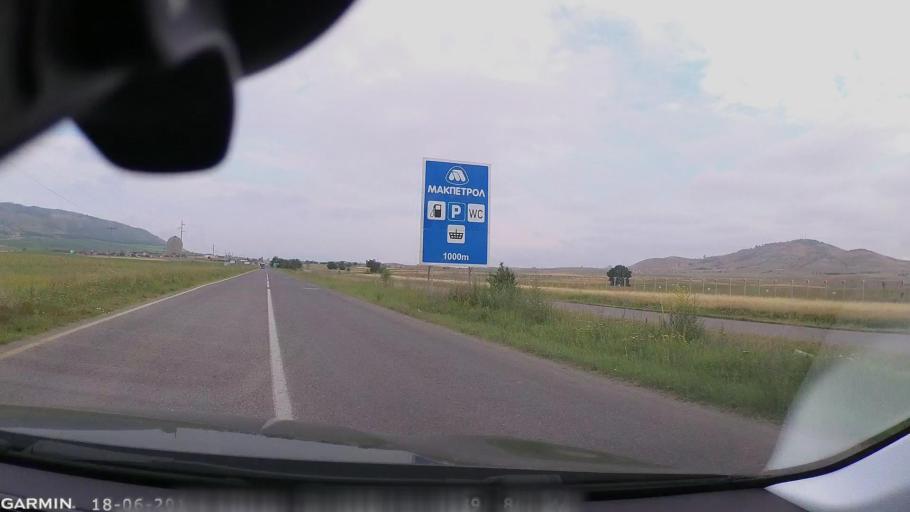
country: MK
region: Stip
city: Shtip
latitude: 41.7673
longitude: 22.1529
